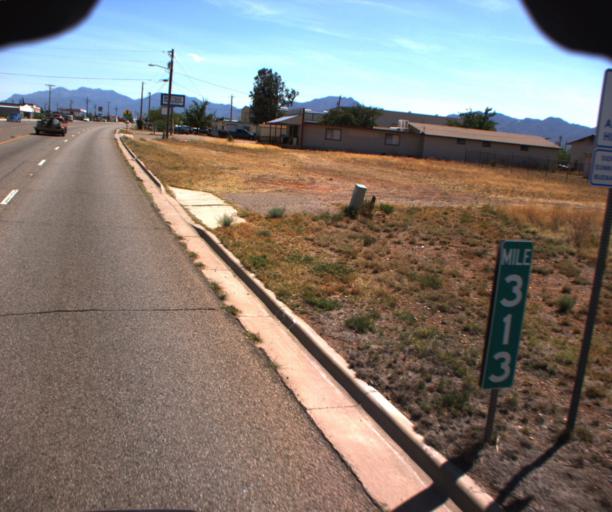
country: US
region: Arizona
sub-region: Cochise County
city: Huachuca City
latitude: 31.6313
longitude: -110.3357
